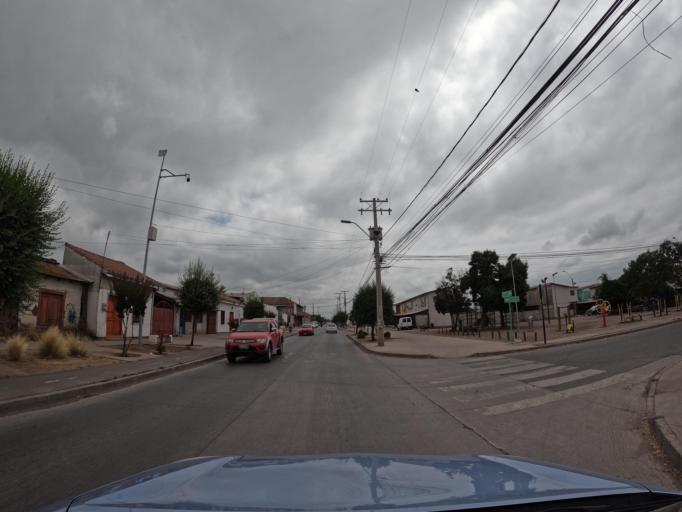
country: CL
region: O'Higgins
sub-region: Provincia de Colchagua
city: Chimbarongo
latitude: -34.7143
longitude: -71.0476
